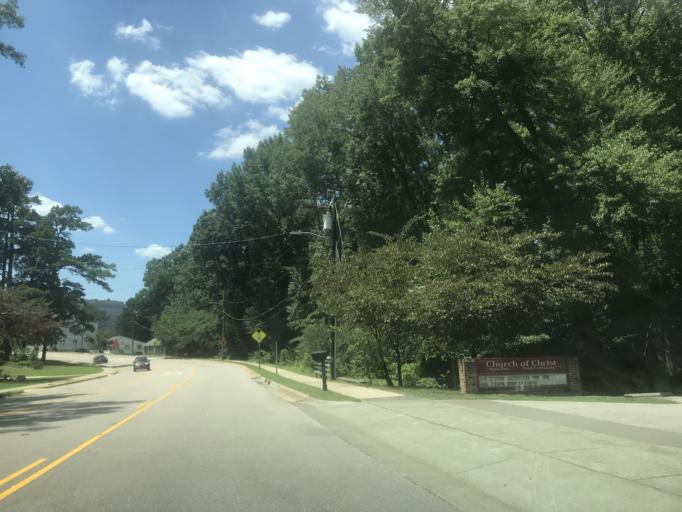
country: US
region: North Carolina
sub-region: Wake County
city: Cary
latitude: 35.7818
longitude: -78.7763
